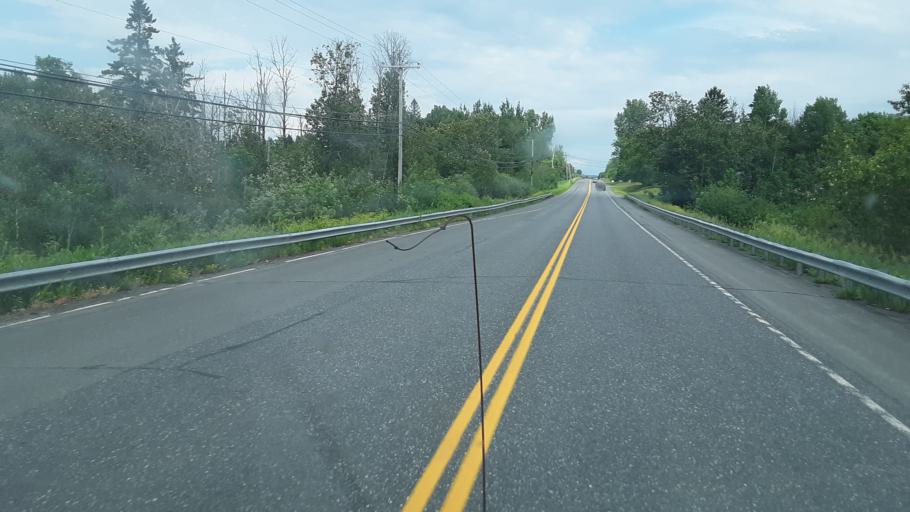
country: US
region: Maine
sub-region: Aroostook County
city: Fort Fairfield
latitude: 46.7607
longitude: -67.8576
